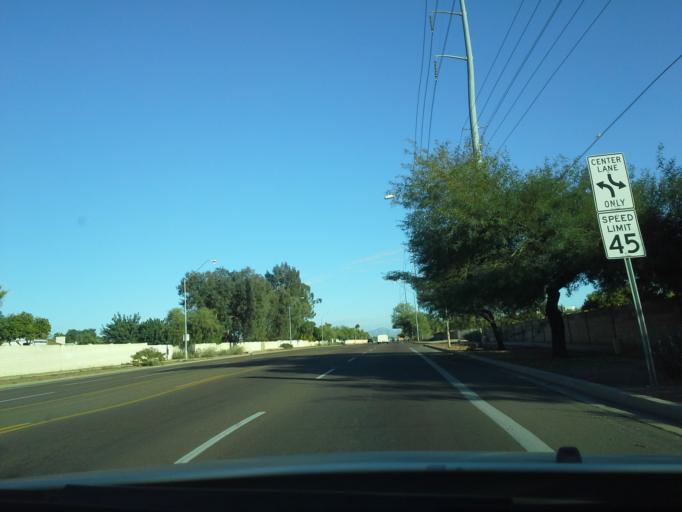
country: US
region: Arizona
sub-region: Maricopa County
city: Glendale
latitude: 33.6545
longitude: -112.1250
